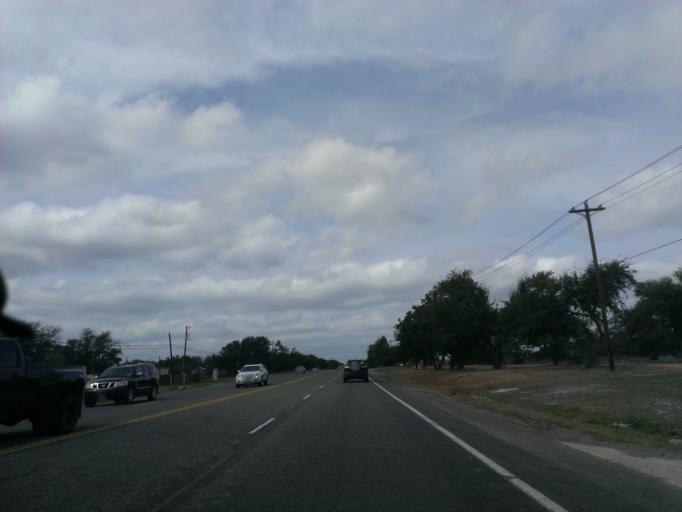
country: US
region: Texas
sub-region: Burnet County
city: Marble Falls
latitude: 30.4827
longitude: -98.2006
